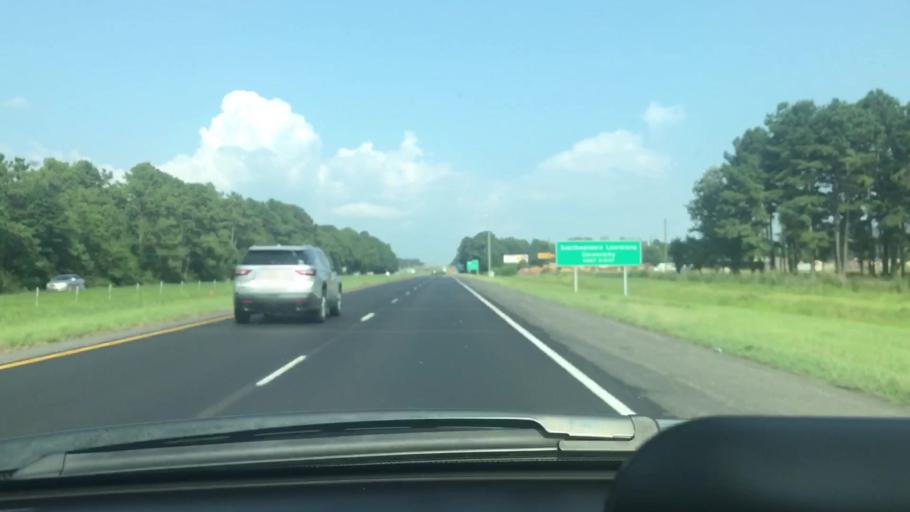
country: US
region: Louisiana
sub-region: Tangipahoa Parish
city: Hammond
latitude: 30.4788
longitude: -90.4723
